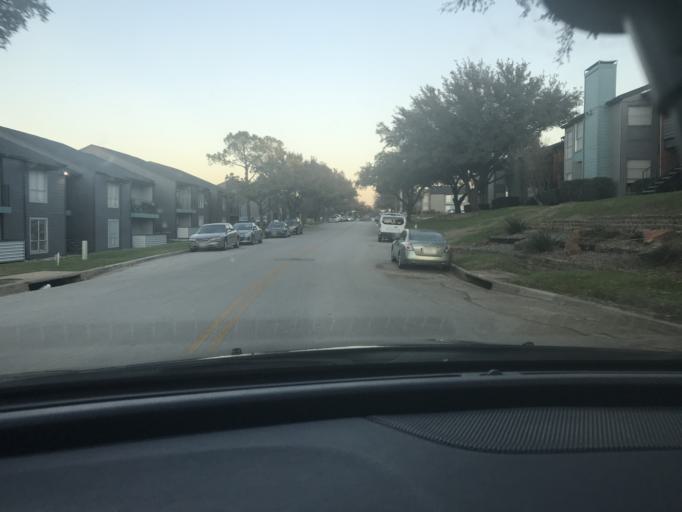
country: US
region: Texas
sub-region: Tarrant County
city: Arlington
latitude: 32.7661
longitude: -97.1031
